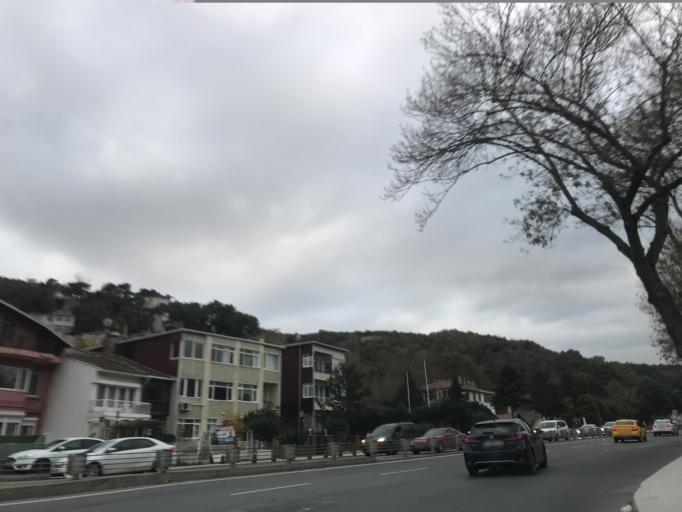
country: TR
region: Istanbul
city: Arikoey
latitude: 41.1539
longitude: 29.0370
